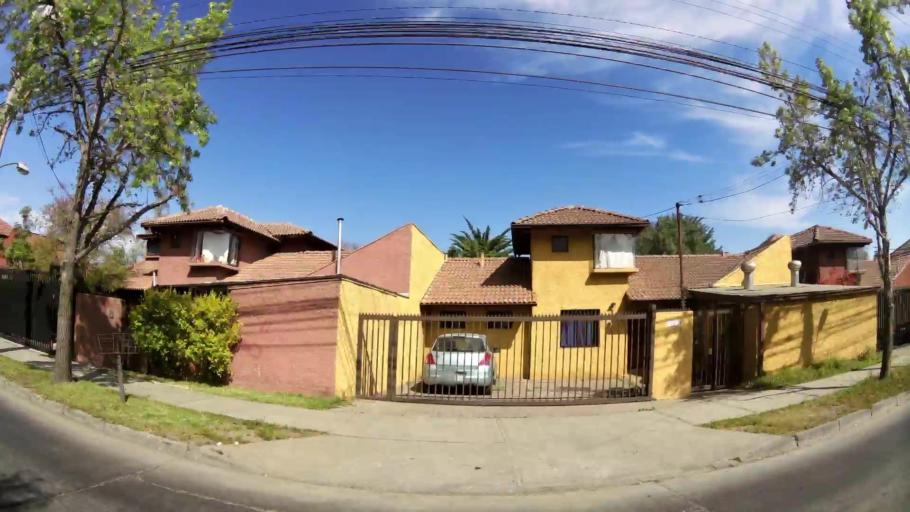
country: CL
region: Santiago Metropolitan
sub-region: Provincia de Santiago
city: Villa Presidente Frei, Nunoa, Santiago, Chile
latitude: -33.4367
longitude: -70.5371
